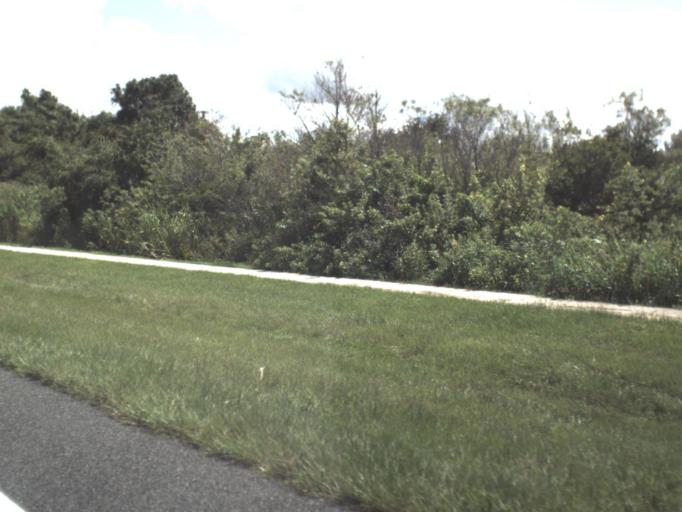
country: US
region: Florida
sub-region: Sarasota County
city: The Meadows
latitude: 27.4318
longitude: -82.4097
